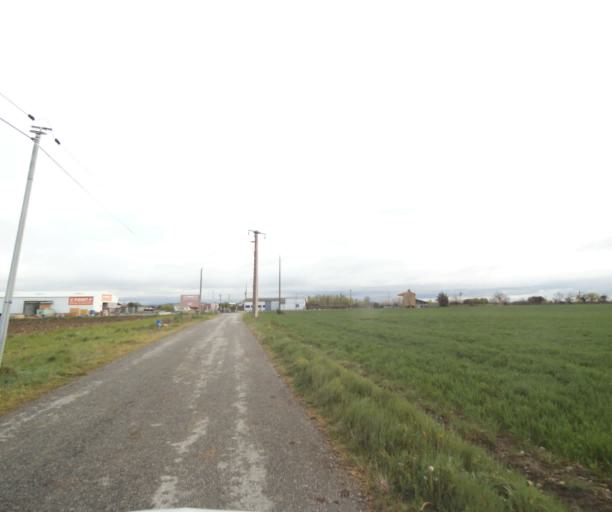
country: FR
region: Midi-Pyrenees
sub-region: Departement de l'Ariege
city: Saverdun
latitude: 43.2314
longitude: 1.5948
